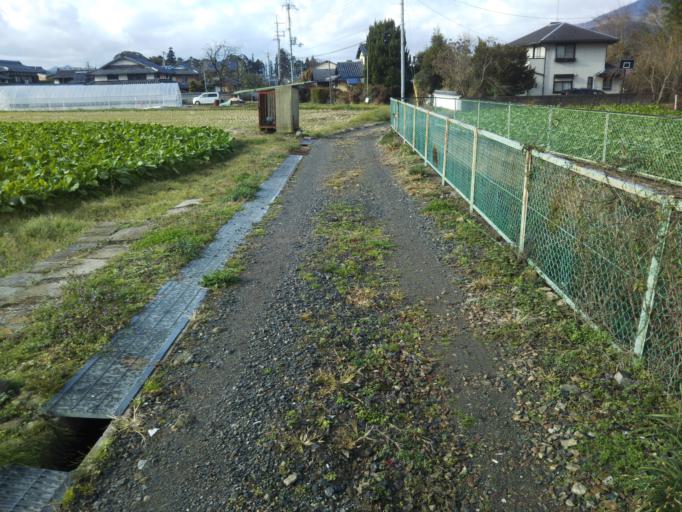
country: JP
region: Kyoto
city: Kameoka
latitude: 35.0003
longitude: 135.6147
